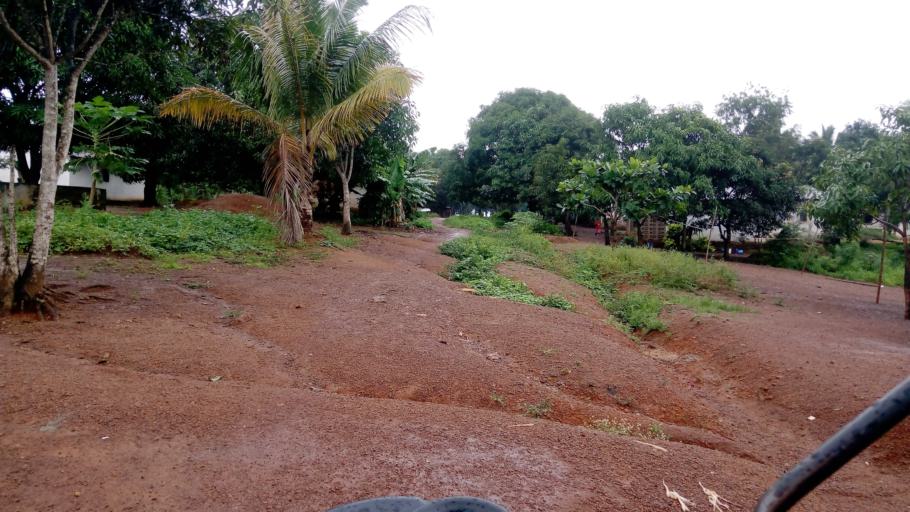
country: SL
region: Southern Province
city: Rotifunk
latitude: 8.4873
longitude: -12.7548
